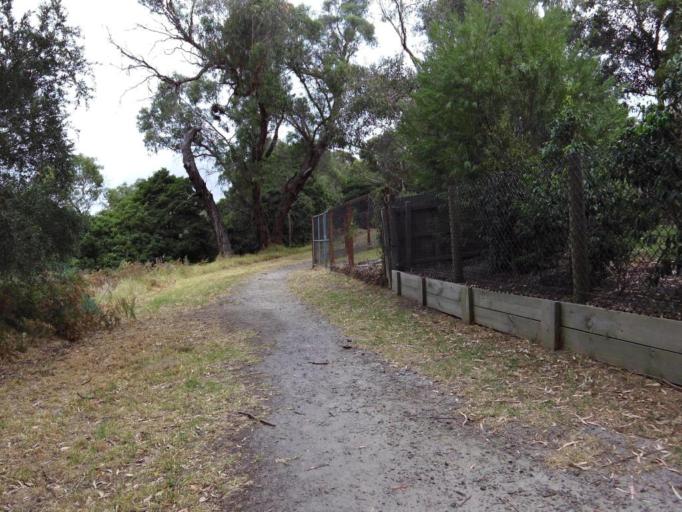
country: AU
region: Victoria
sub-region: Frankston
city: Frankston
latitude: -38.1635
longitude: 145.1110
